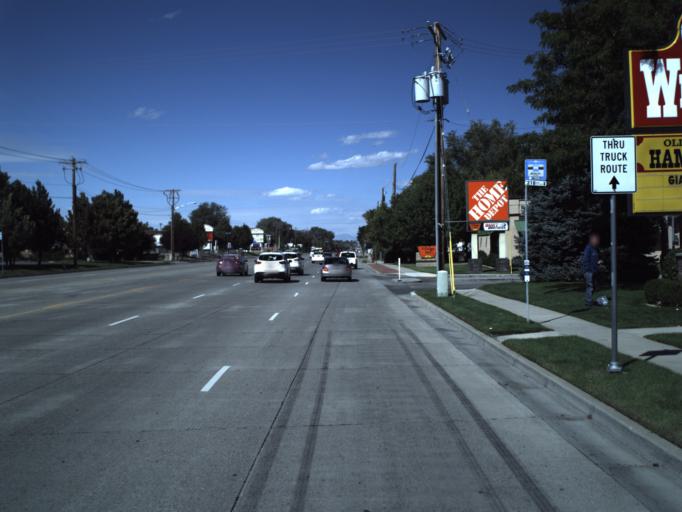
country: US
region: Utah
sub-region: Salt Lake County
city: West Jordan
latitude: 40.5888
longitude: -111.9386
